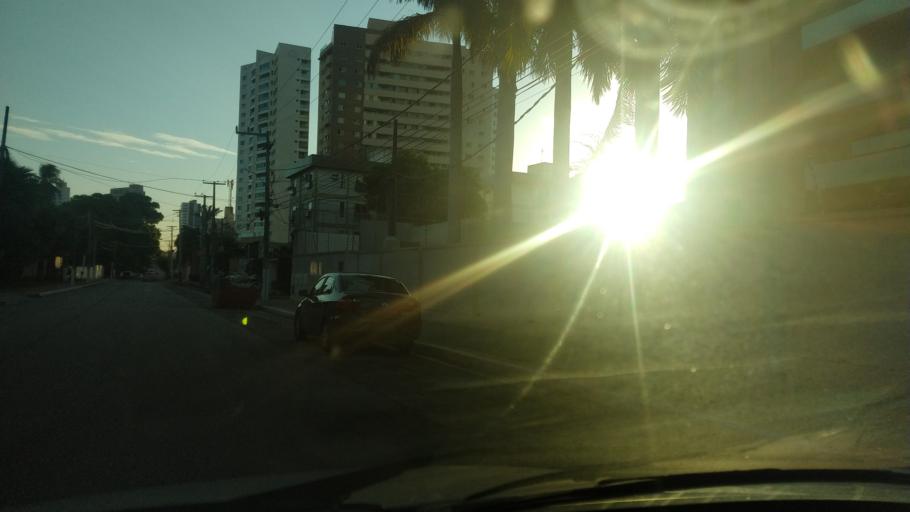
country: BR
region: Rio Grande do Norte
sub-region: Natal
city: Natal
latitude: -5.8583
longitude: -35.1969
